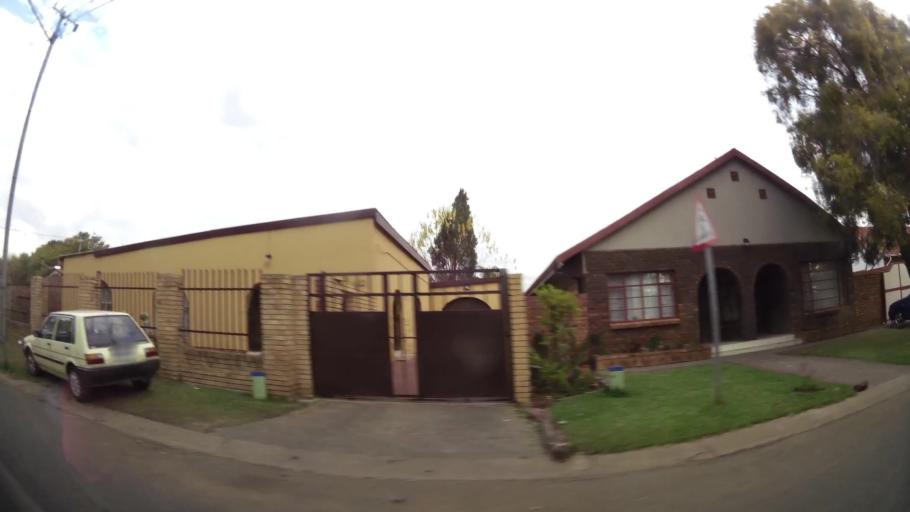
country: ZA
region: Gauteng
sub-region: City of Tshwane Metropolitan Municipality
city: Pretoria
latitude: -25.7131
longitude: 28.3112
